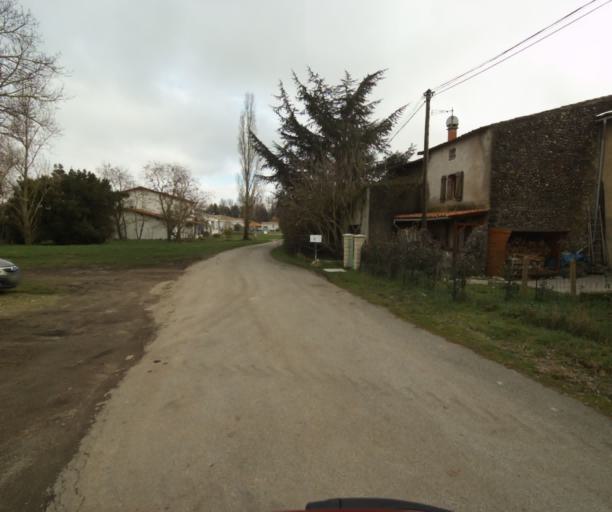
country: FR
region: Languedoc-Roussillon
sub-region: Departement de l'Aude
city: Belpech
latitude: 43.1710
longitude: 1.6883
